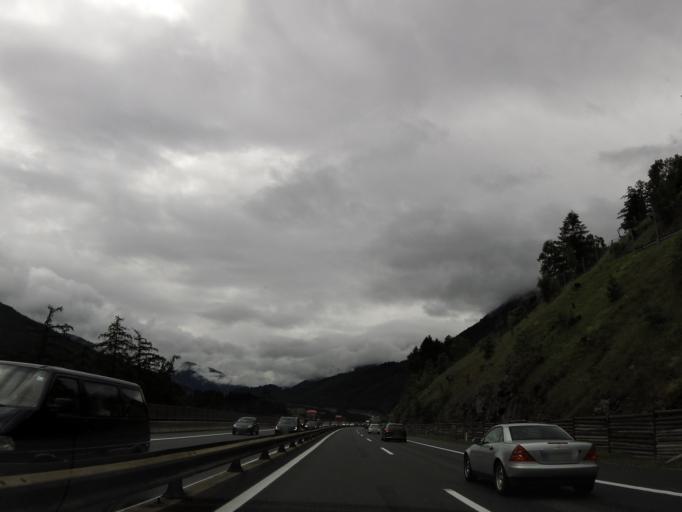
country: AT
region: Tyrol
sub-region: Politischer Bezirk Innsbruck Land
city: Matrei am Brenner
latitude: 47.1286
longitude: 11.4499
